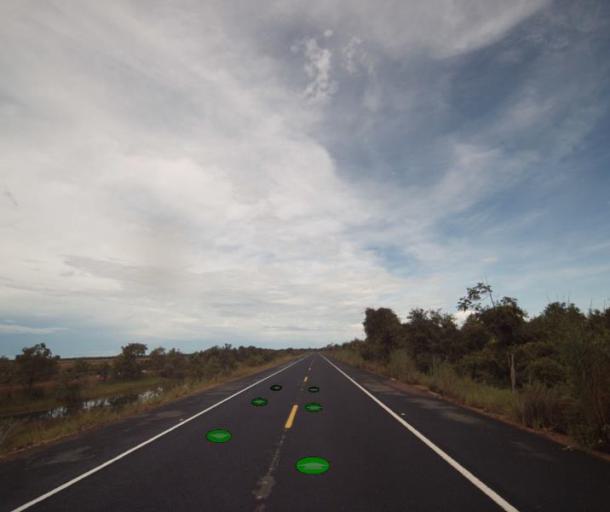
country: BR
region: Goias
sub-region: Sao Miguel Do Araguaia
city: Sao Miguel do Araguaia
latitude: -13.2377
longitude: -50.5501
